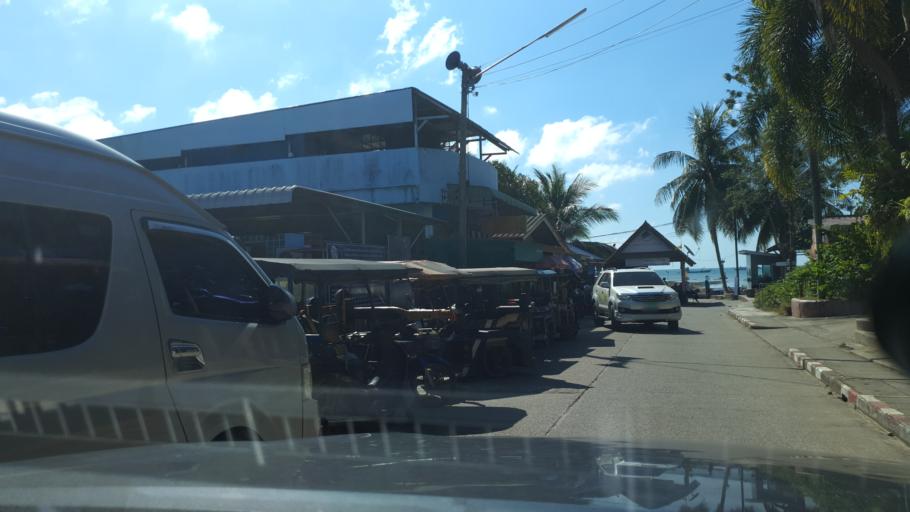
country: TH
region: Phangnga
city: Ban Ao Nang
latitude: 8.0297
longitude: 98.8630
